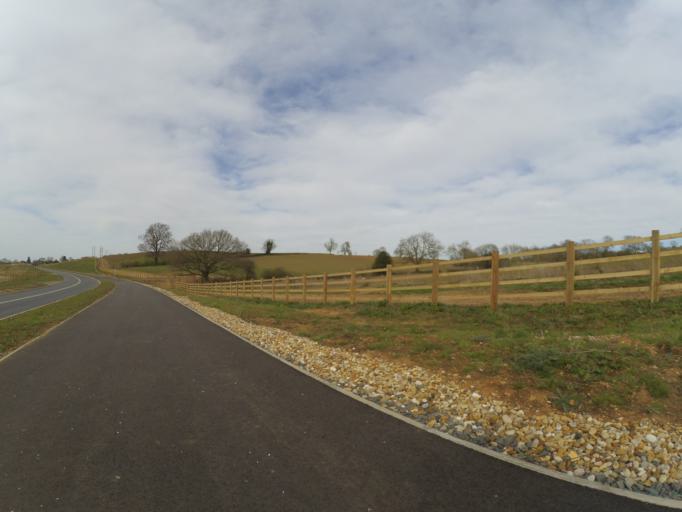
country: GB
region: England
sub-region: Warwickshire
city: Rugby
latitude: 52.3746
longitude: -1.2255
